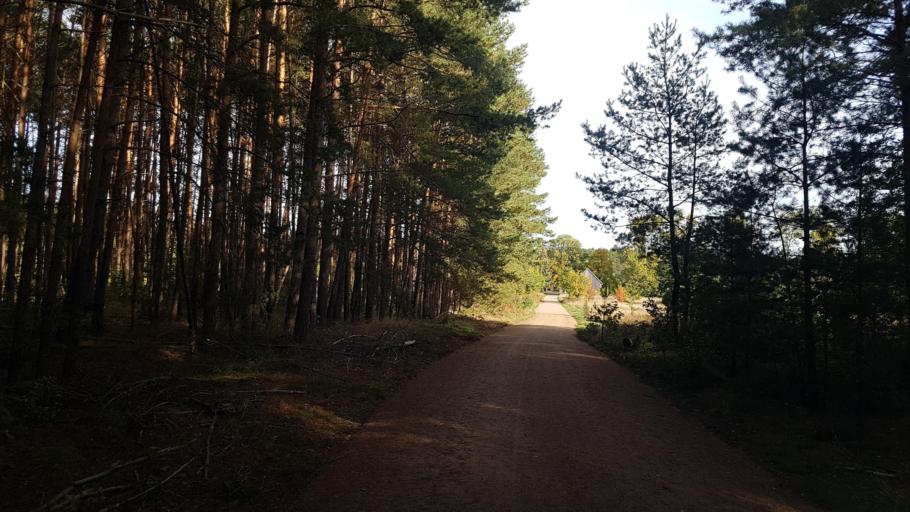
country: DE
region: Brandenburg
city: Hohenbucko
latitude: 51.8156
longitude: 13.5290
